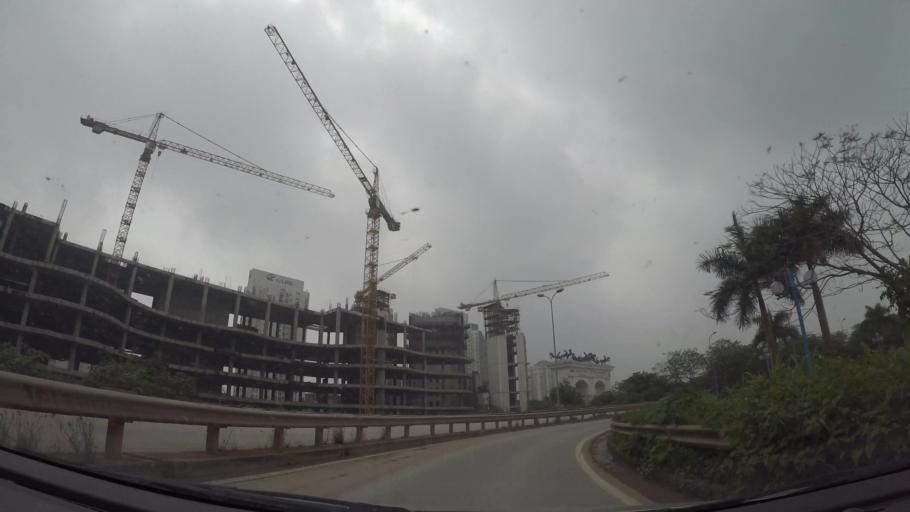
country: VN
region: Ha Noi
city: Tay Ho
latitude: 21.0826
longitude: 105.7893
